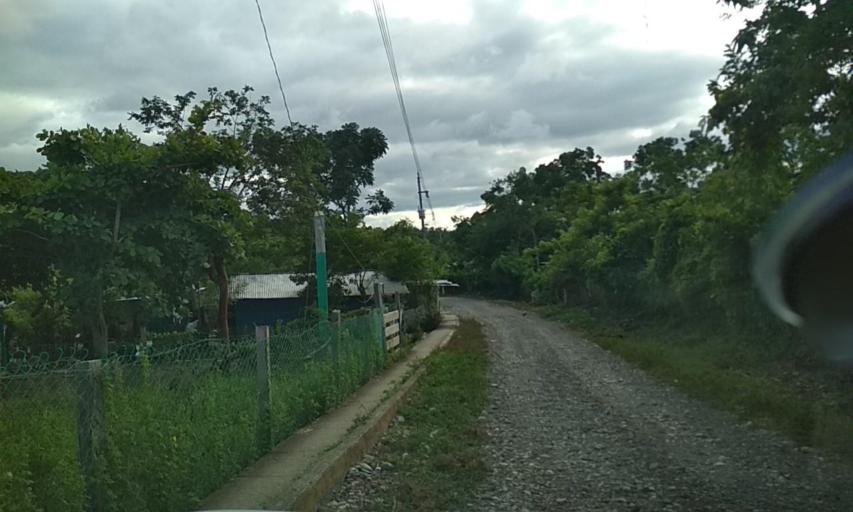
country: MX
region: Veracruz
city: Cazones de Herrera
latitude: 20.6493
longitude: -97.3375
